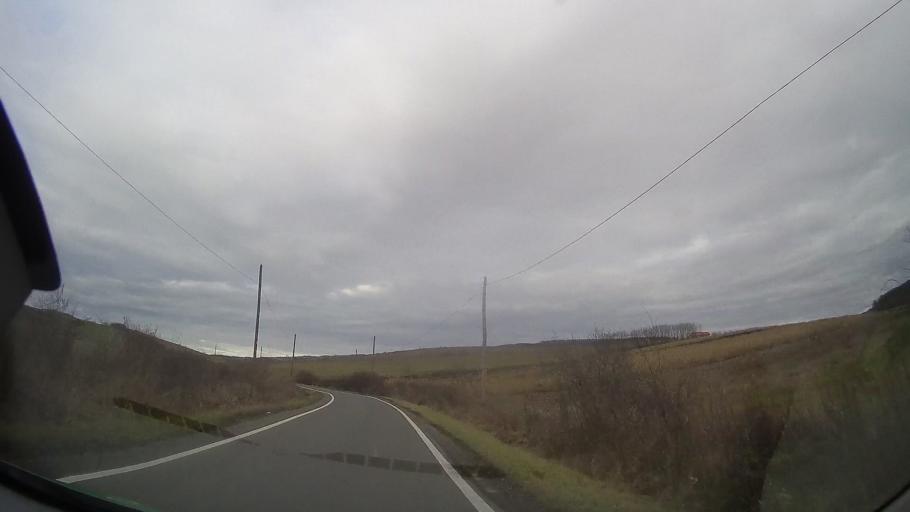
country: RO
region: Mures
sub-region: Comuna Cozma
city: Cozma
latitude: 46.7888
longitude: 24.5464
